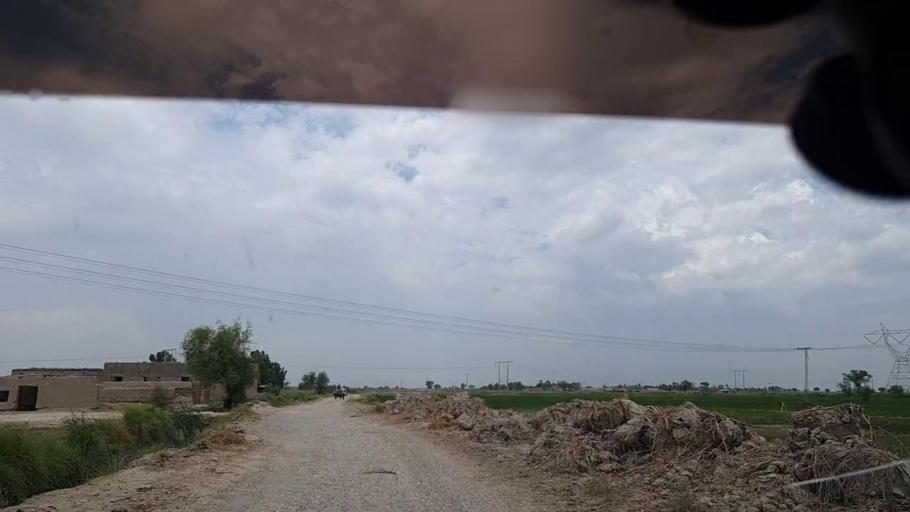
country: PK
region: Sindh
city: Ghauspur
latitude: 28.1090
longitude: 68.9861
